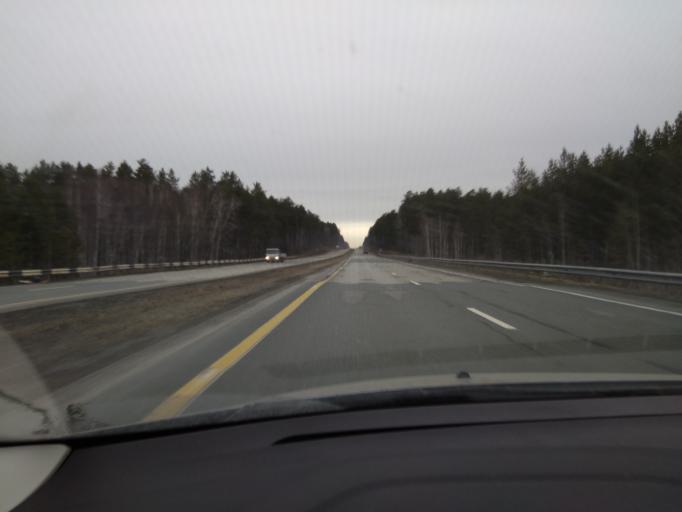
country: RU
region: Sverdlovsk
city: Sysert'
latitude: 56.4255
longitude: 60.8746
